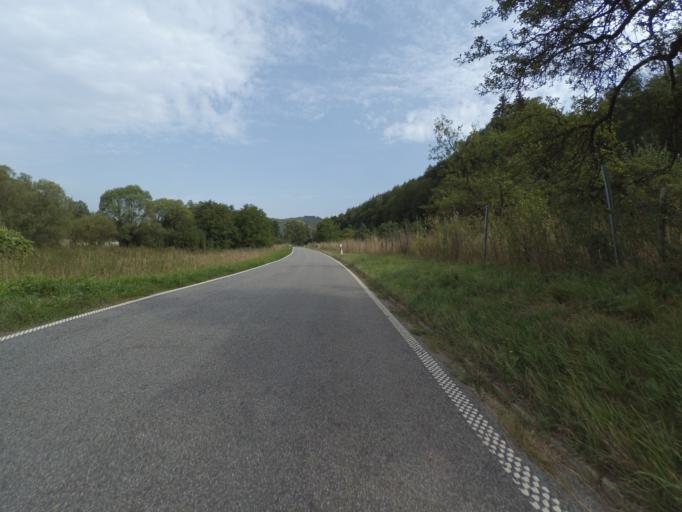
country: DE
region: Rheinland-Pfalz
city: Tawern
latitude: 49.6648
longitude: 6.5151
